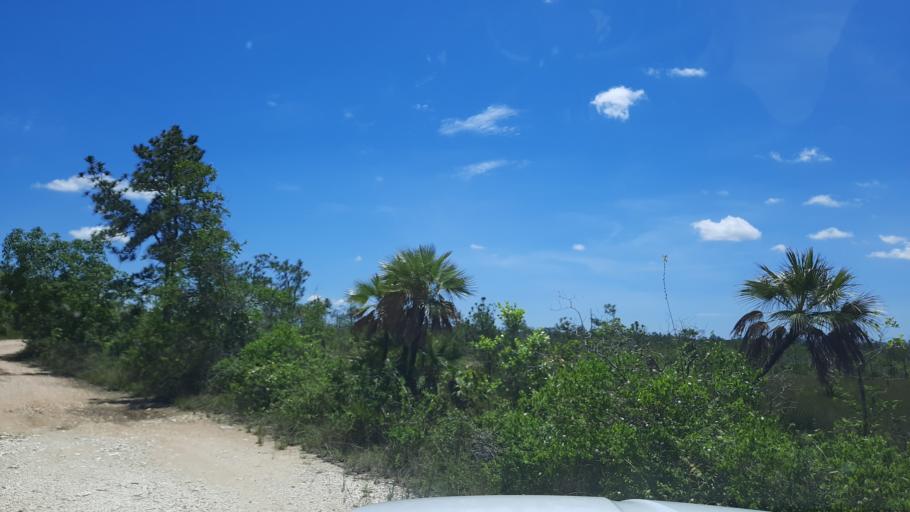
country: BZ
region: Cayo
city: Belmopan
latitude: 17.3535
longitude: -88.5499
